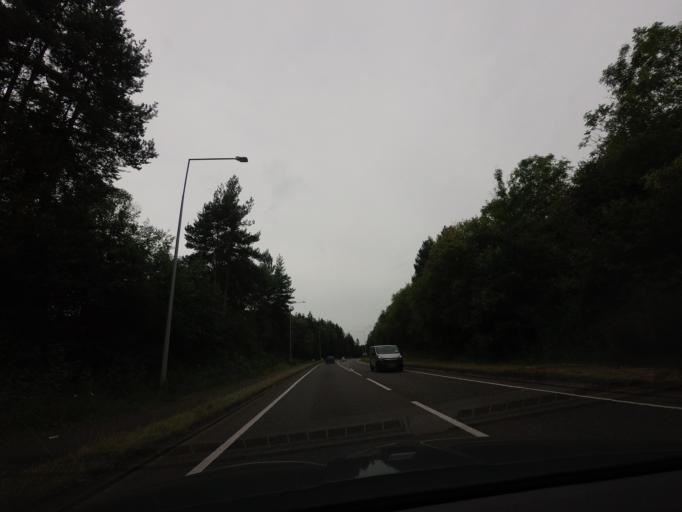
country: GB
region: England
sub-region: Telford and Wrekin
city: Ironbridge
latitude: 52.6437
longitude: -2.4758
